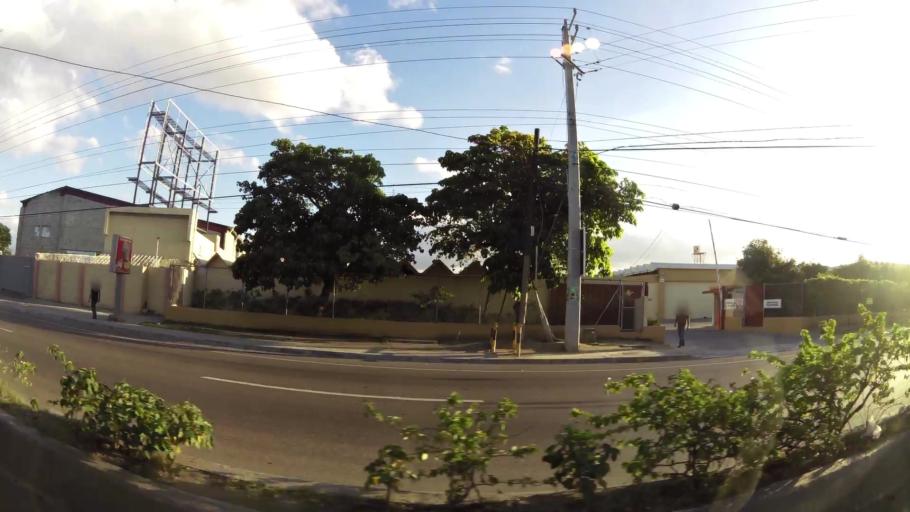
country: DO
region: Santiago
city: Santiago de los Caballeros
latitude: 19.4899
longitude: -70.7212
